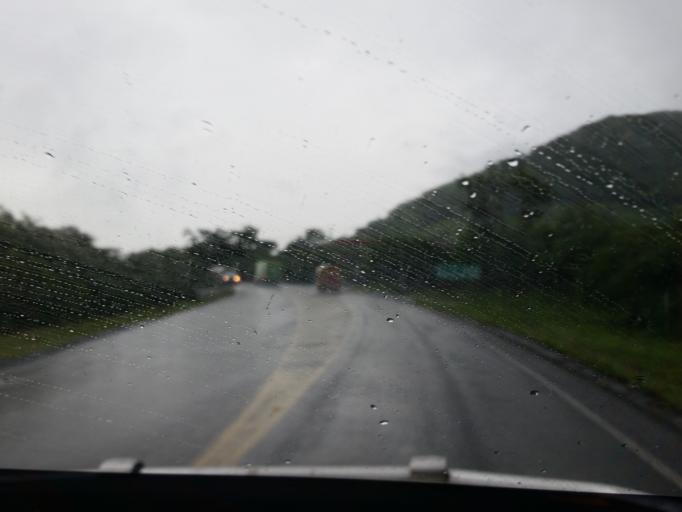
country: NI
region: Matagalpa
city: Matagalpa
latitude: 12.9223
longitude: -86.0085
